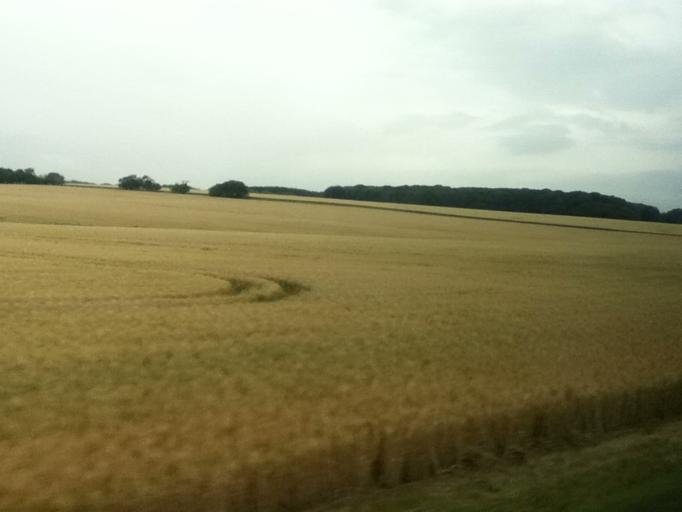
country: DE
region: Thuringia
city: Umpferstedt
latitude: 50.9723
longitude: 11.4156
